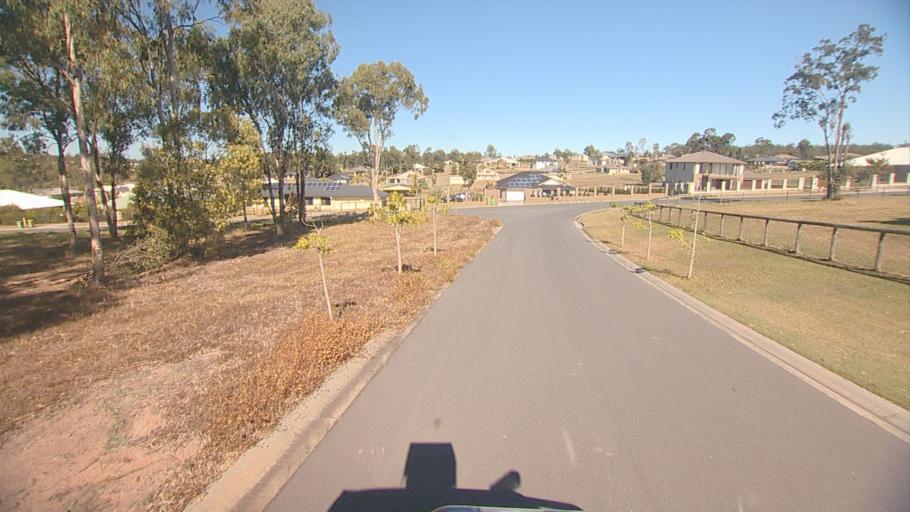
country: AU
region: Queensland
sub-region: Logan
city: North Maclean
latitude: -27.7521
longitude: 152.9476
